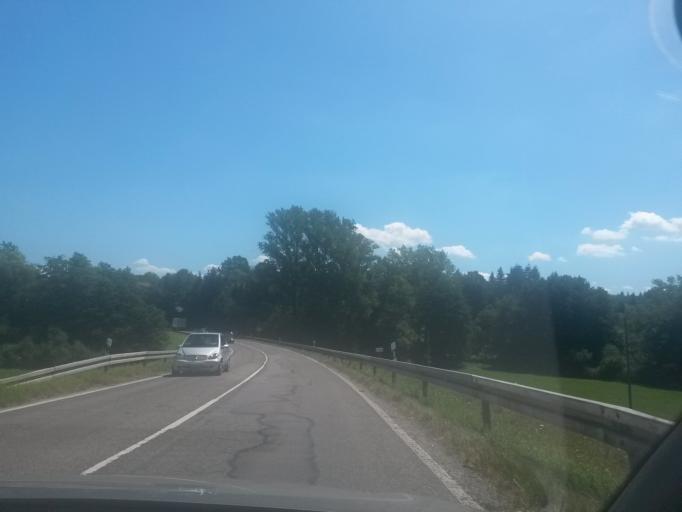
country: DE
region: Baden-Wuerttemberg
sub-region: Karlsruhe Region
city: Neuenburg
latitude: 48.9109
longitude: 8.5237
